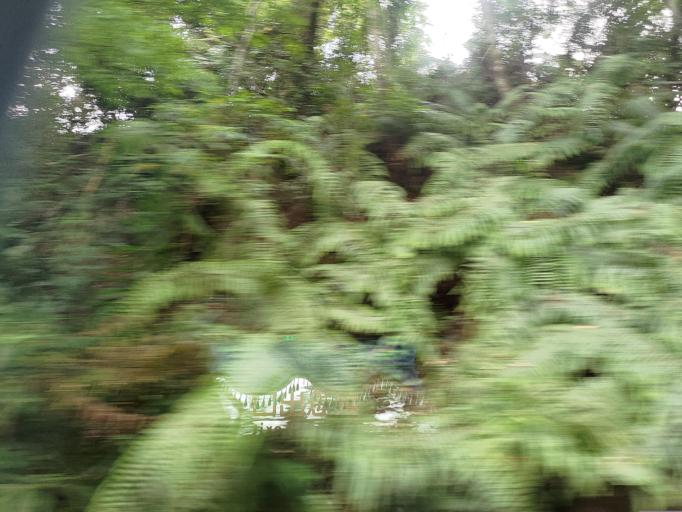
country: TW
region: Taiwan
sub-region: Hsinchu
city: Hsinchu
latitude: 24.6201
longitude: 121.0452
